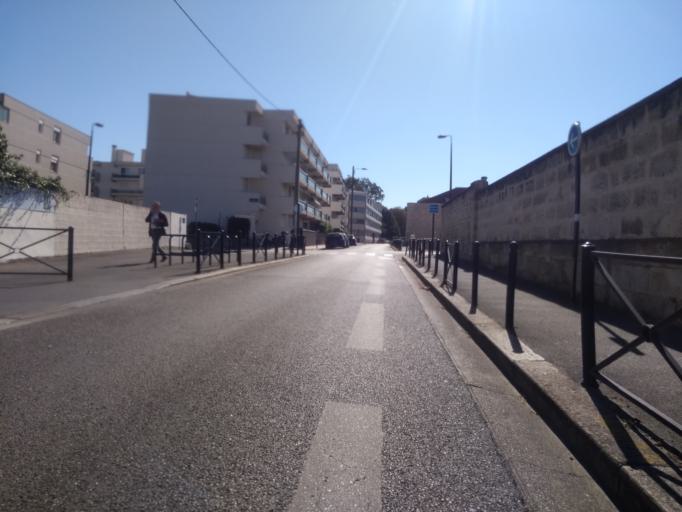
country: FR
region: Aquitaine
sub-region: Departement de la Gironde
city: Le Bouscat
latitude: 44.8570
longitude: -0.5889
